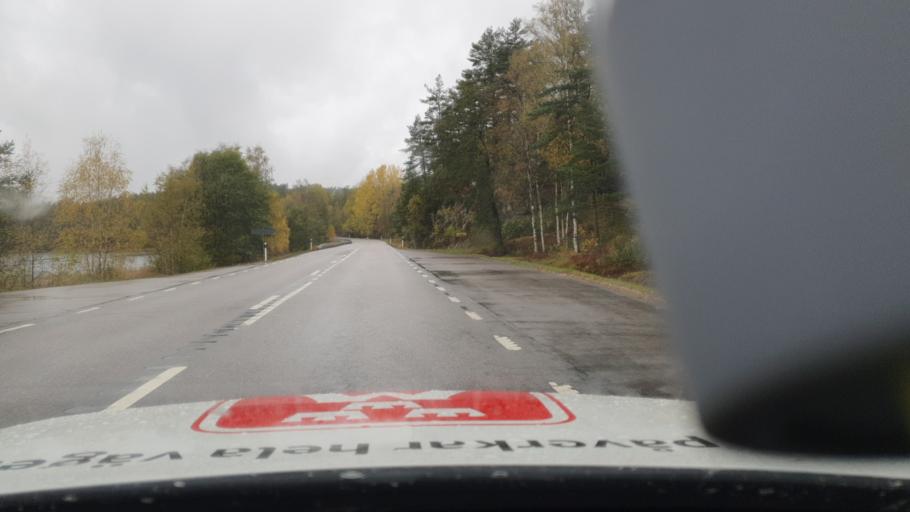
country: SE
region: Vaestra Goetaland
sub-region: Dals-Ed Kommun
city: Ed
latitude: 58.8781
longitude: 11.8292
